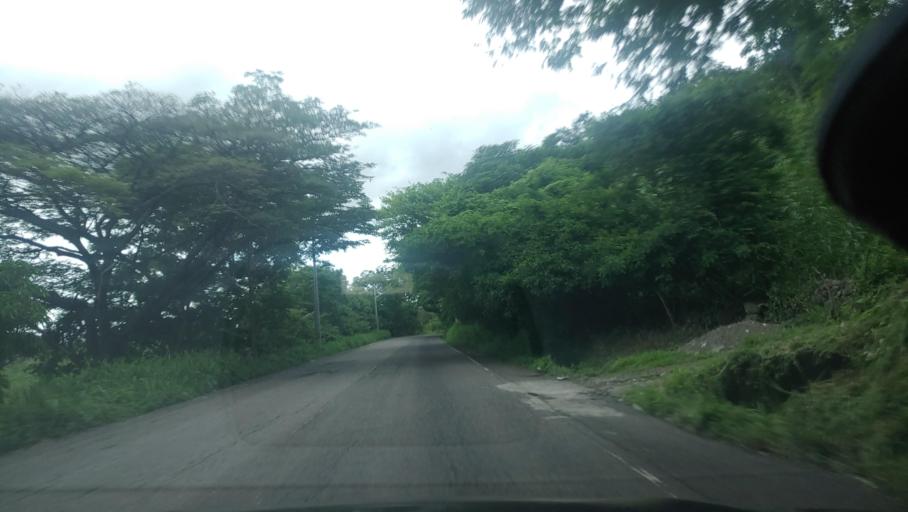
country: HN
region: Choluteca
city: Corpus
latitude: 13.3748
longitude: -87.0452
